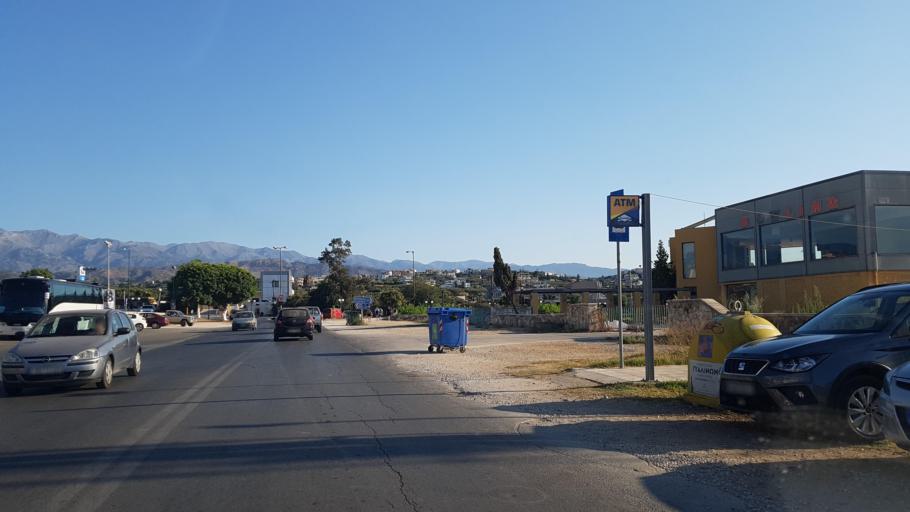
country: GR
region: Crete
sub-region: Nomos Chanias
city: Daratsos
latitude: 35.5085
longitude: 23.9820
